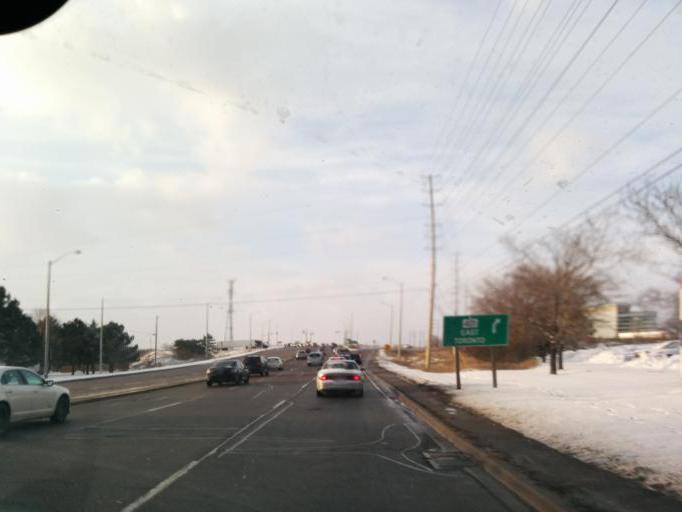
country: CA
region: Ontario
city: Brampton
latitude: 43.6030
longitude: -79.7424
